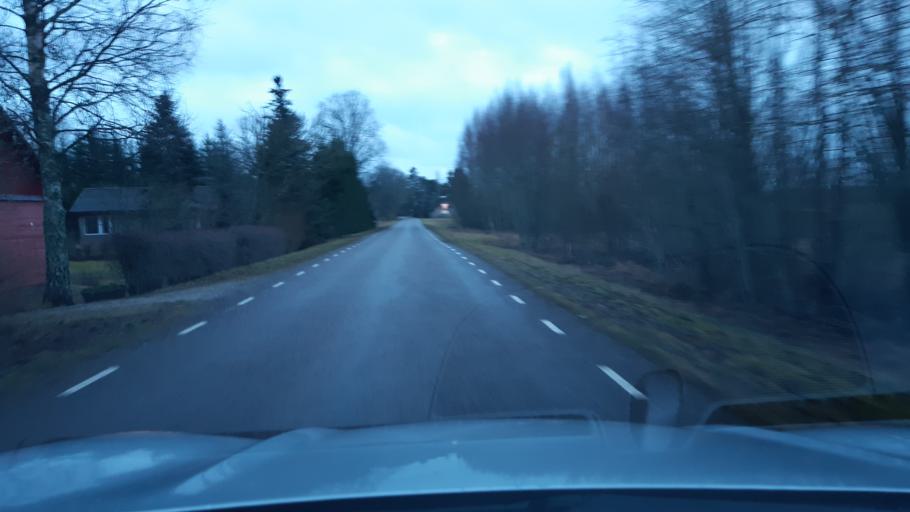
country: EE
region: Raplamaa
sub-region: Rapla vald
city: Rapla
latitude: 58.9834
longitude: 24.7349
